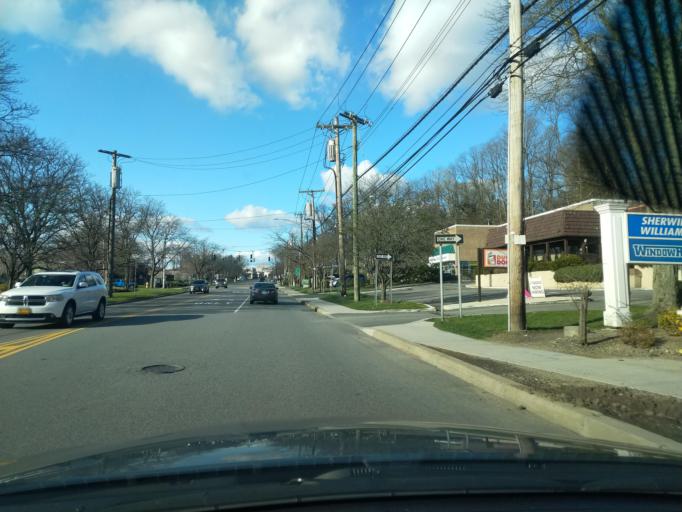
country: US
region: New York
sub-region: Westchester County
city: Mount Kisco
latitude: 41.2140
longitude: -73.7203
